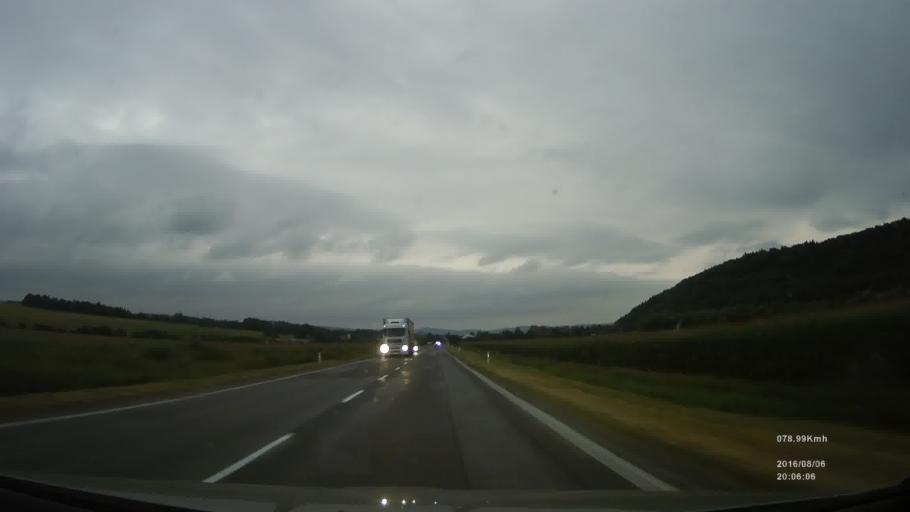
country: SK
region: Presovsky
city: Stropkov
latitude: 49.2293
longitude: 21.6302
